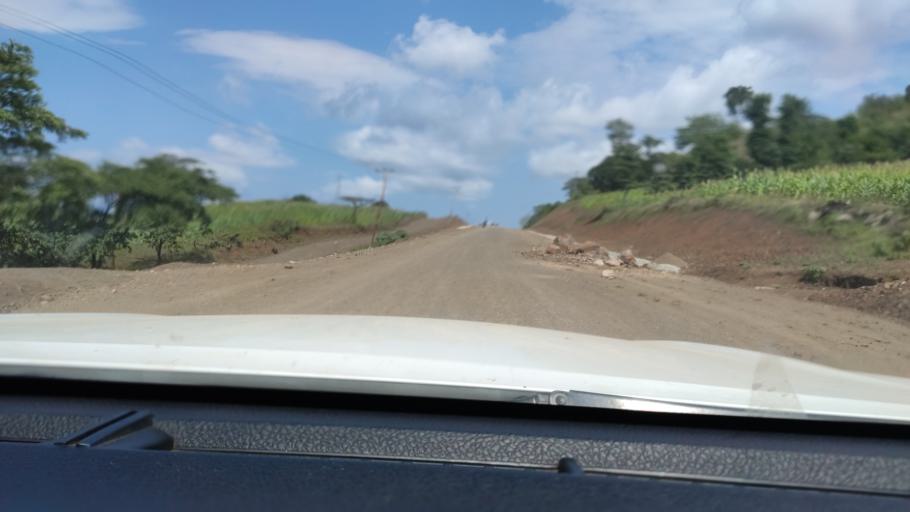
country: ET
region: Southern Nations, Nationalities, and People's Region
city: Felege Neway
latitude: 6.3940
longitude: 37.0734
